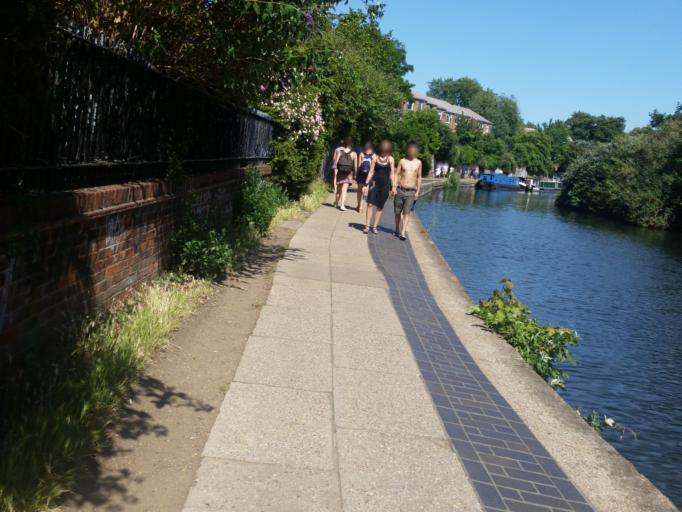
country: GB
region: England
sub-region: Greater London
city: Bethnal Green
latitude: 51.5351
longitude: -0.0552
